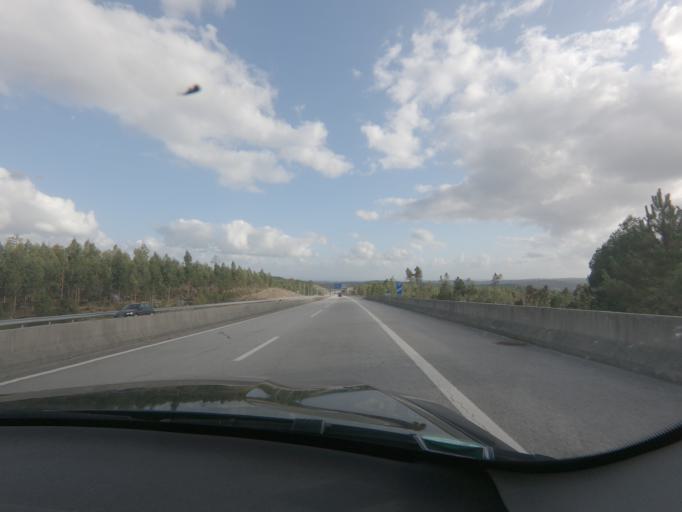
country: PT
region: Viseu
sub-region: Viseu
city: Abraveses
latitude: 40.6831
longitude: -7.9680
